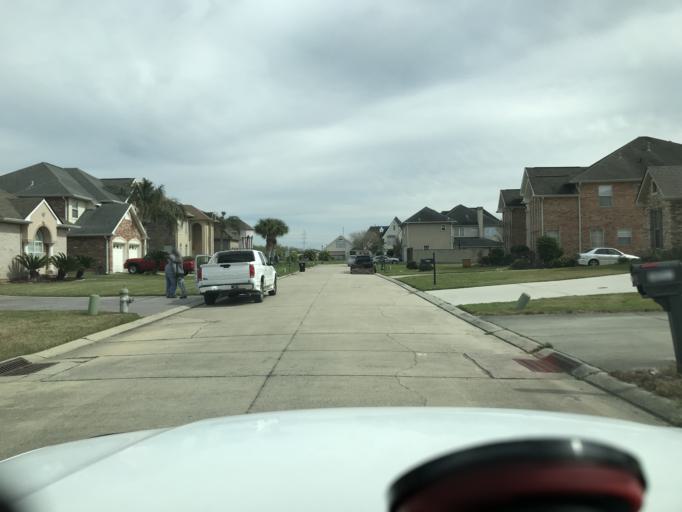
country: US
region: Louisiana
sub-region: Saint Bernard Parish
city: Chalmette
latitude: 30.0327
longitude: -89.9468
